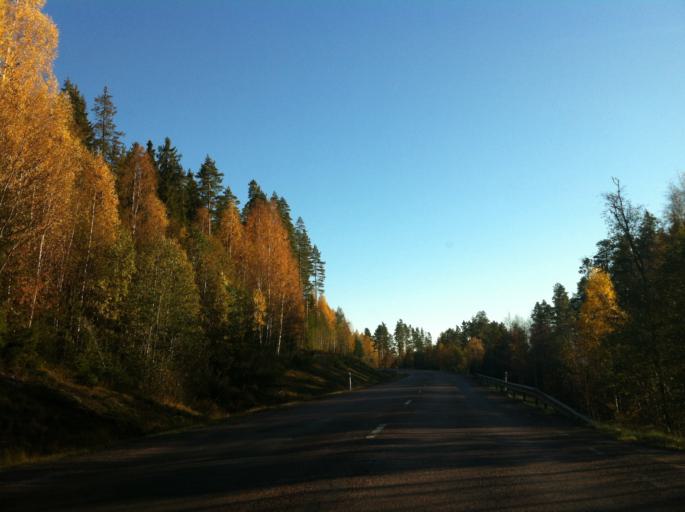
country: SE
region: Dalarna
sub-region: Faluns Kommun
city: Bjursas
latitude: 60.7667
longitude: 15.3186
